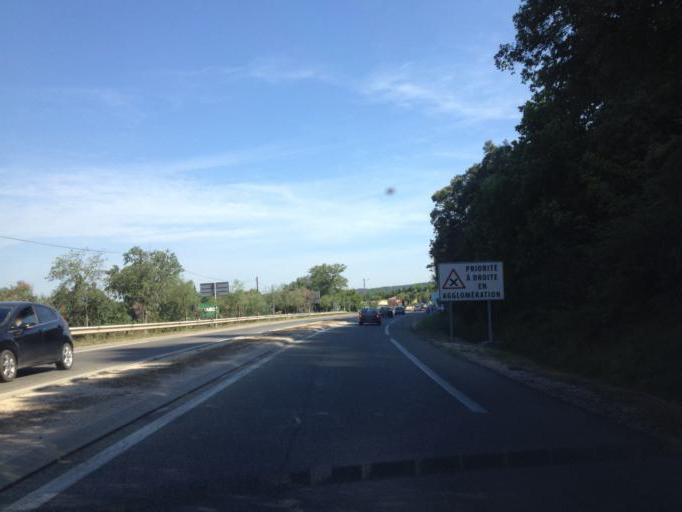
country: FR
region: Provence-Alpes-Cote d'Azur
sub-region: Departement du Vaucluse
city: Piolenc
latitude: 44.1716
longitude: 4.7617
